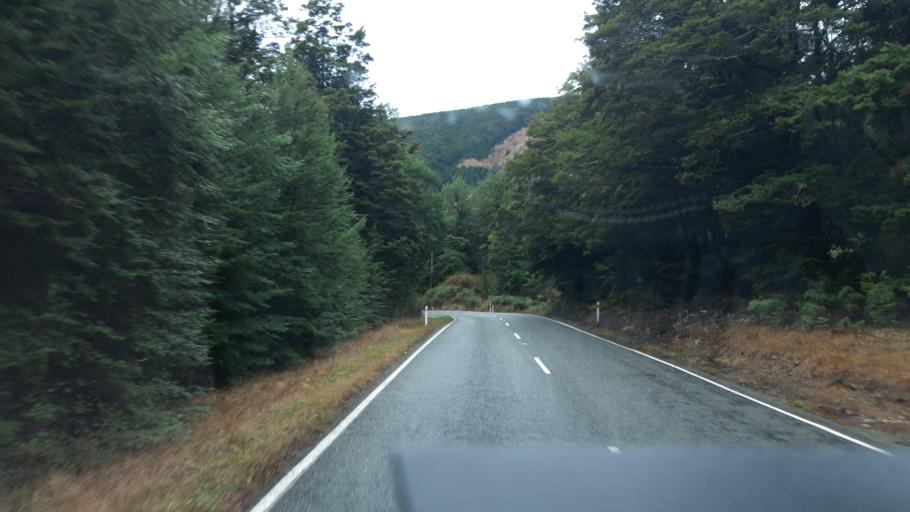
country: NZ
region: Tasman
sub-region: Tasman District
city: Wakefield
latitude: -41.7601
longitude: 172.8977
